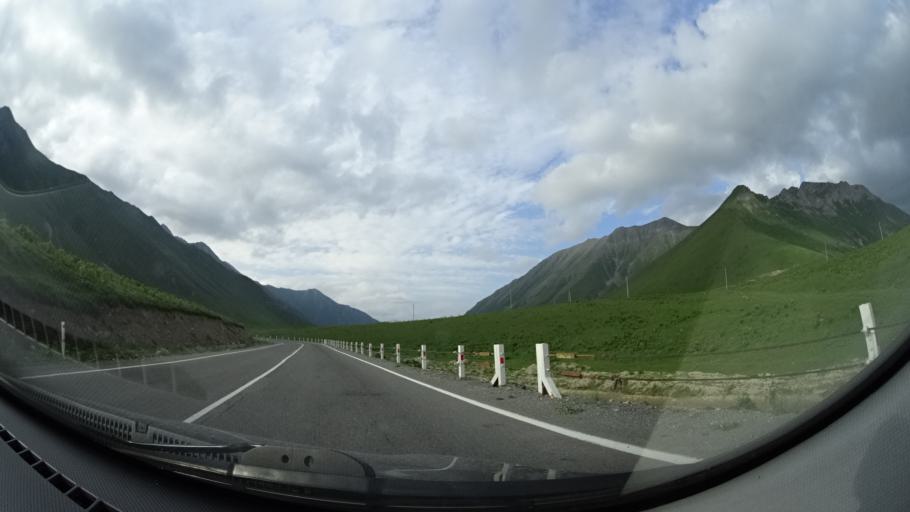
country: GE
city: Gudauri
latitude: 42.5016
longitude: 44.4542
